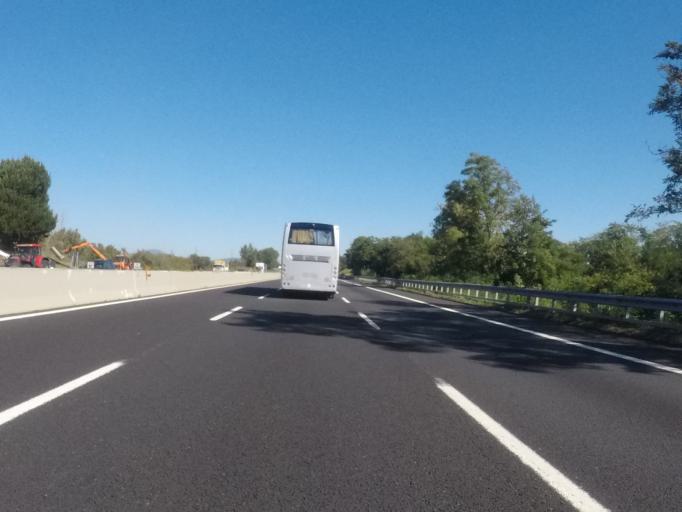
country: IT
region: Campania
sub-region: Provincia di Caserta
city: Teano
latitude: 41.2452
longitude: 14.0924
